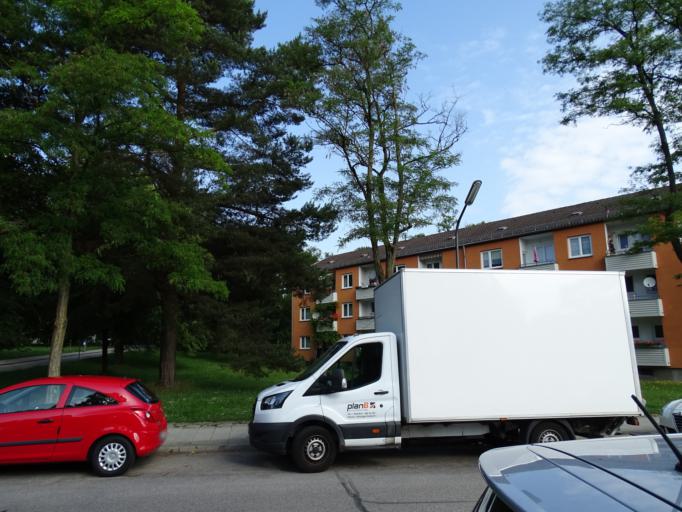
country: DE
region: Bavaria
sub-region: Upper Bavaria
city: Oberschleissheim
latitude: 48.2154
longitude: 11.5599
